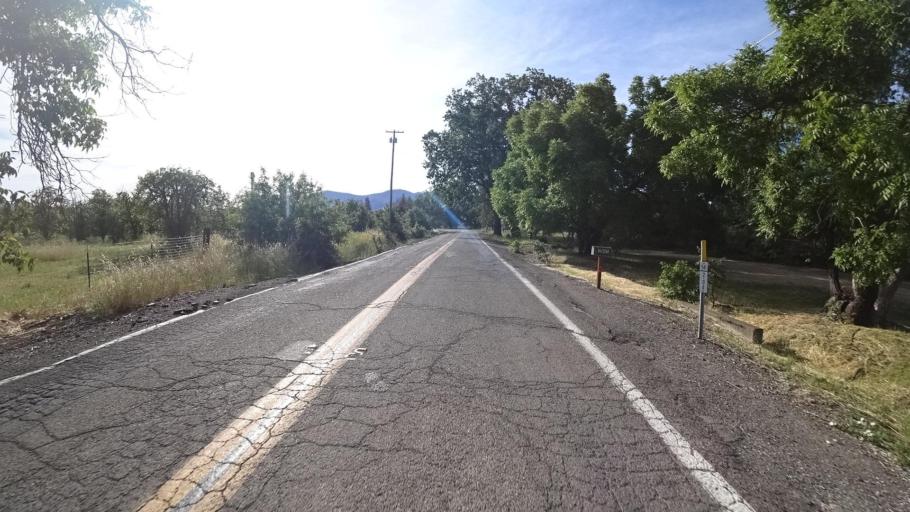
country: US
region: California
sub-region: Lake County
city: Kelseyville
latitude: 38.9976
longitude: -122.8729
